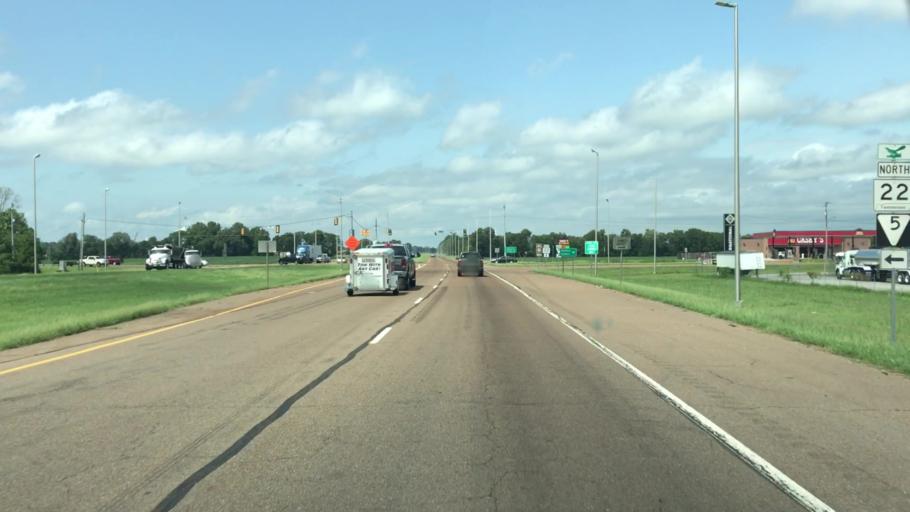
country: US
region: Tennessee
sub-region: Obion County
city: Union City
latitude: 36.4256
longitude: -89.0674
